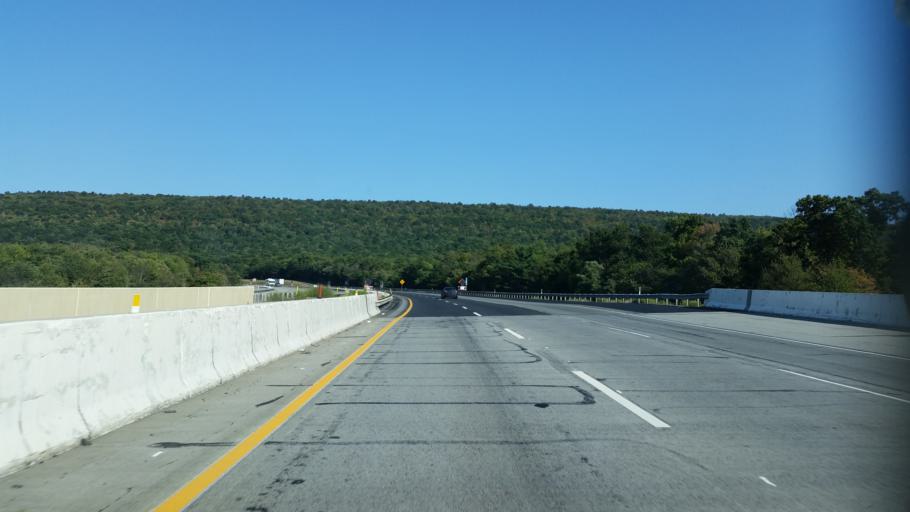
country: US
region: Pennsylvania
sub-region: Bedford County
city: Earlston
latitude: 39.9852
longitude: -78.2434
